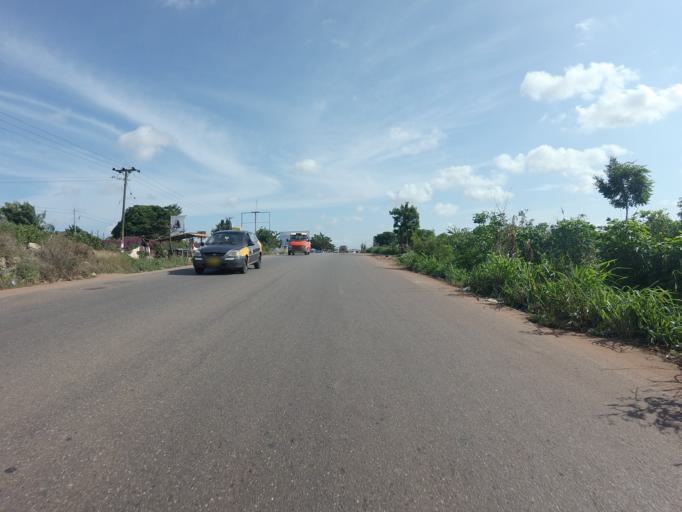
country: GH
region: Greater Accra
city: Medina Estates
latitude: 5.6489
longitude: -0.1693
